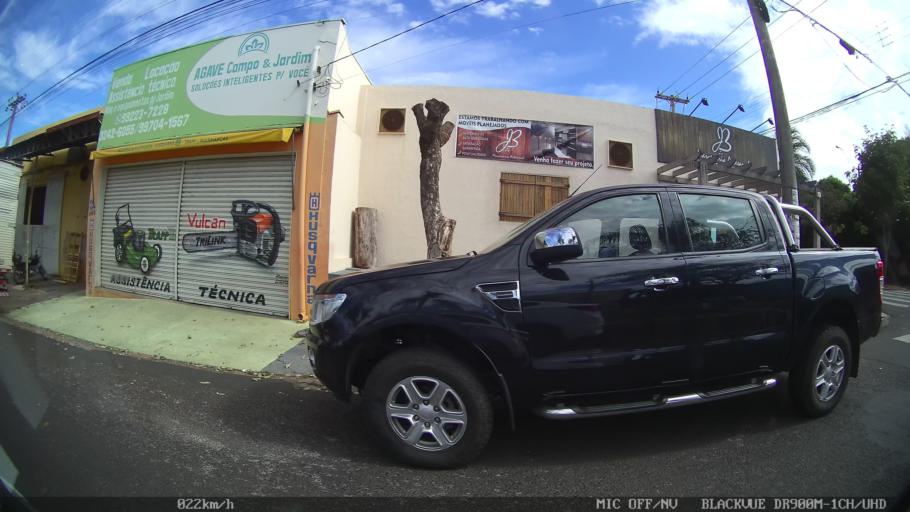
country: BR
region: Sao Paulo
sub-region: Bady Bassitt
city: Bady Bassitt
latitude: -20.8190
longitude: -49.5233
